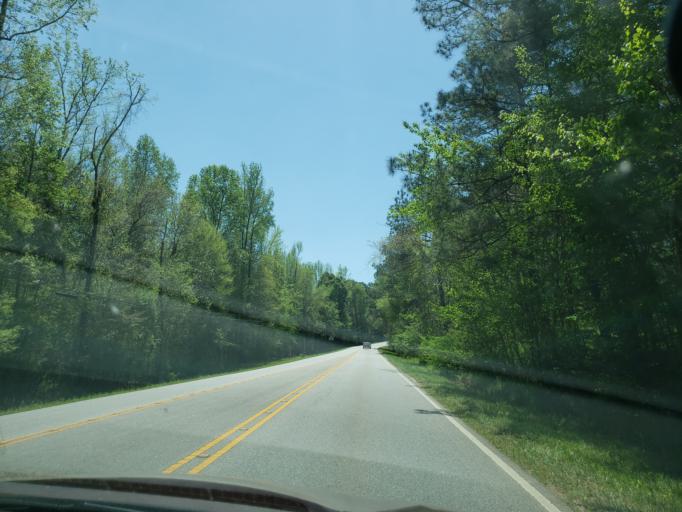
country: US
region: Alabama
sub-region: Lee County
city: Auburn
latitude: 32.6392
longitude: -85.5026
